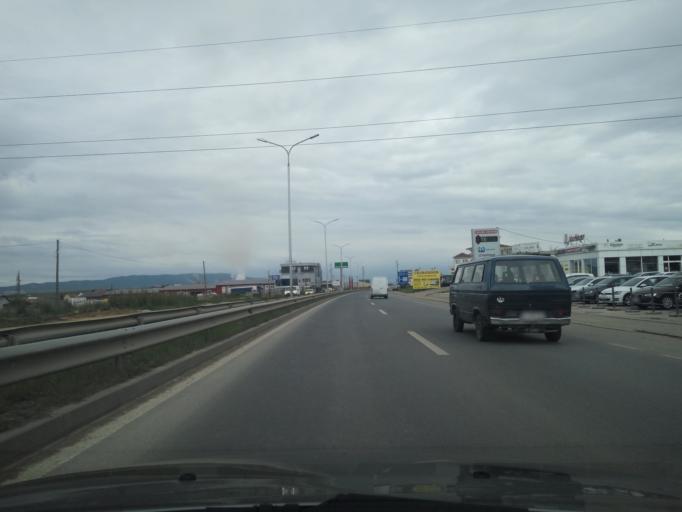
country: XK
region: Pristina
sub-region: Komuna e Prishtines
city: Pristina
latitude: 42.6599
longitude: 21.1336
